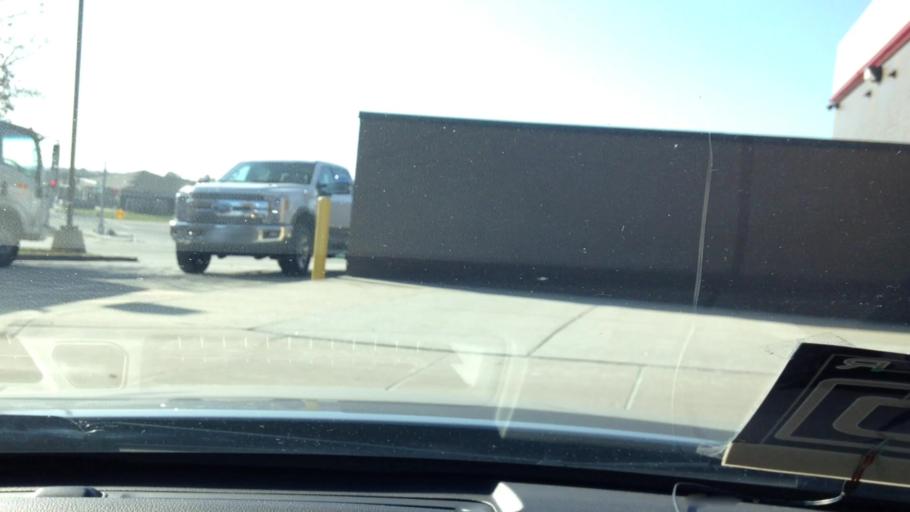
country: US
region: Missouri
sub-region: Platte County
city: Platte City
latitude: 39.3547
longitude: -94.7657
